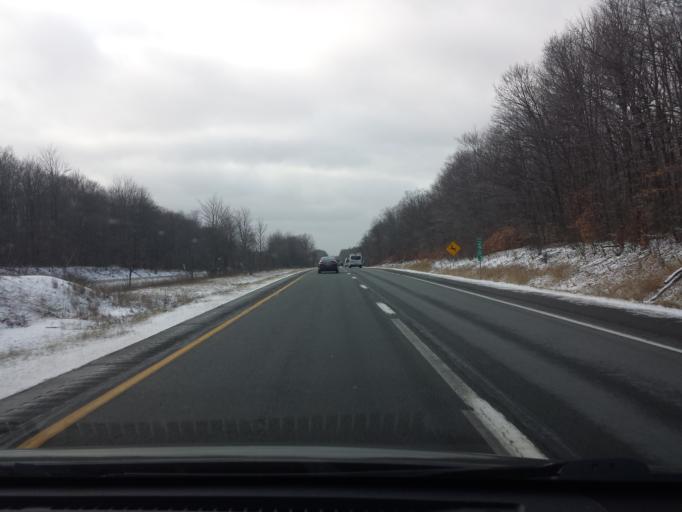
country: US
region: Pennsylvania
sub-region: Monroe County
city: Emerald Lakes
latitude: 41.0718
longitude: -75.4482
